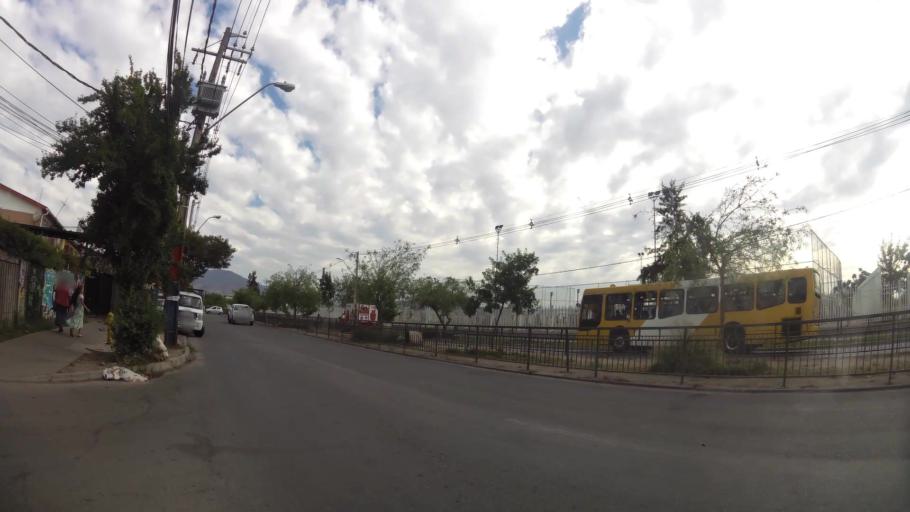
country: CL
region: Santiago Metropolitan
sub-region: Provincia de Cordillera
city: Puente Alto
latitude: -33.6229
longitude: -70.6126
